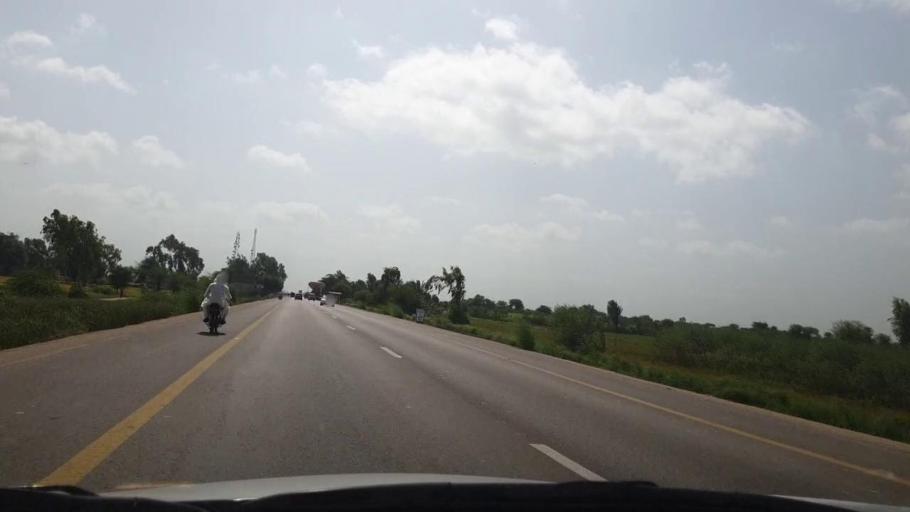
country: PK
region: Sindh
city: Matli
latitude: 24.9441
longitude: 68.7005
